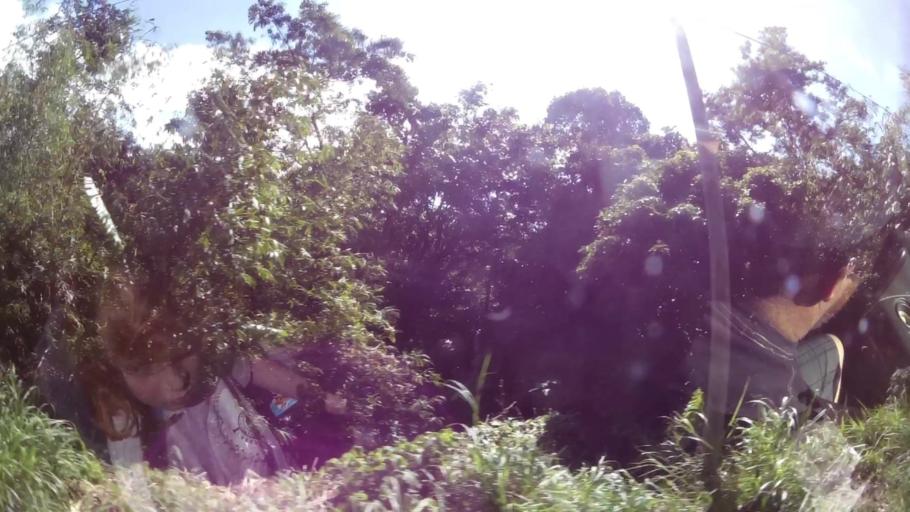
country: DM
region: Saint Paul
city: Pont Casse
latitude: 15.3571
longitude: -61.3562
